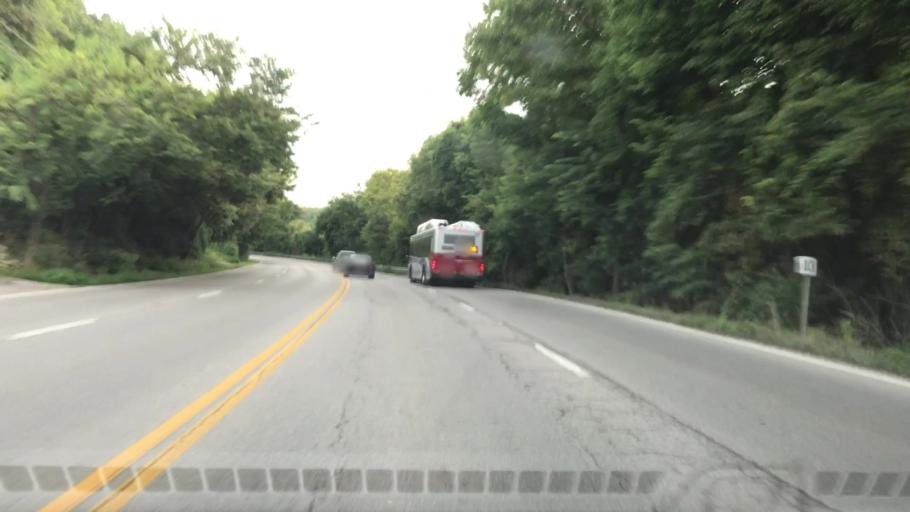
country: US
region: Ohio
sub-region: Franklin County
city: Upper Arlington
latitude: 40.0153
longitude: -83.0906
